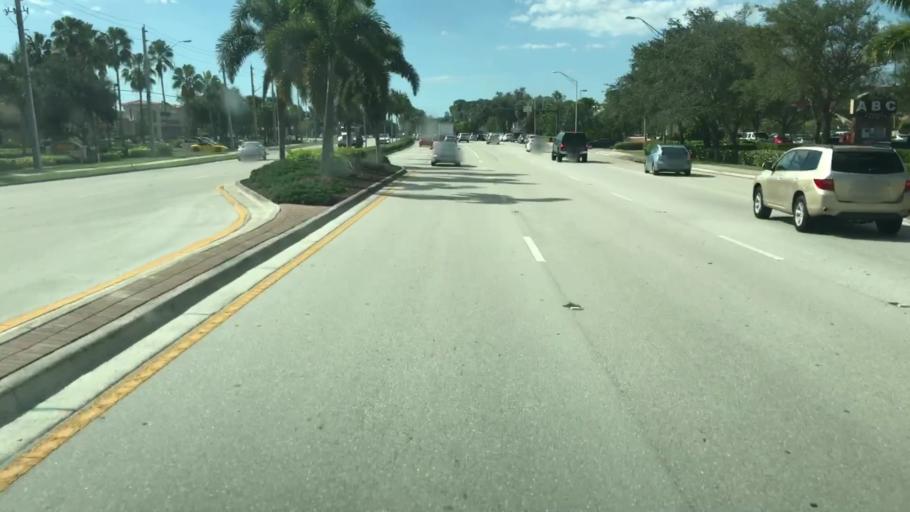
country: US
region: Florida
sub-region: Collier County
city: Naples Park
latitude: 26.2723
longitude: -81.7986
